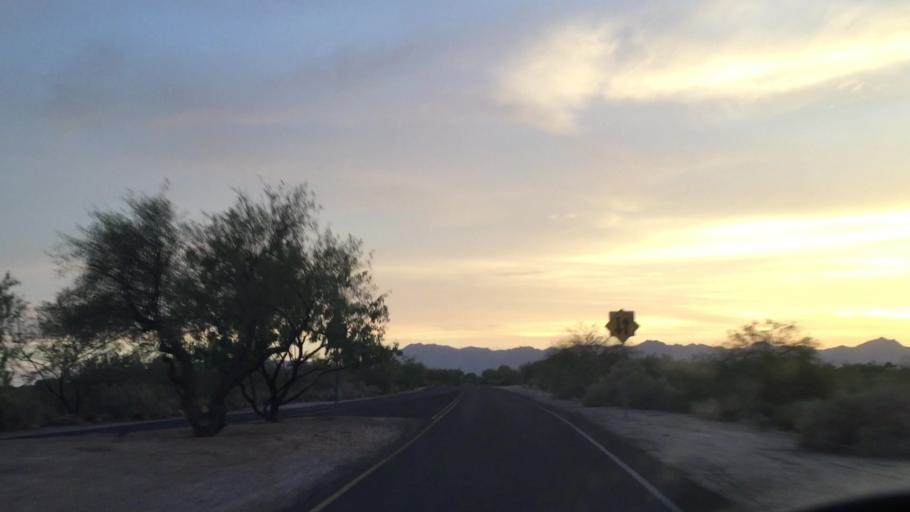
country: US
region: Arizona
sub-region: Maricopa County
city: Guadalupe
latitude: 33.2756
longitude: -111.9828
